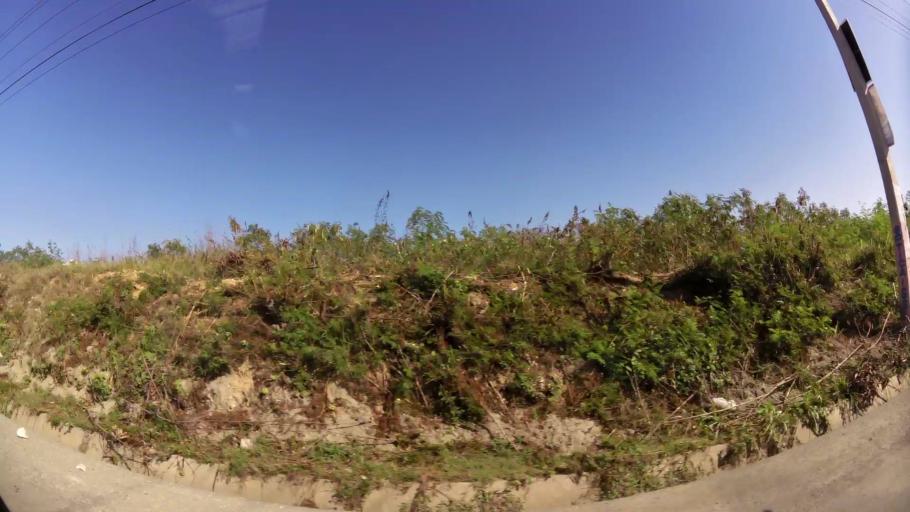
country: DO
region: San Cristobal
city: Bajos de Haina
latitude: 18.4311
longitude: -70.0563
